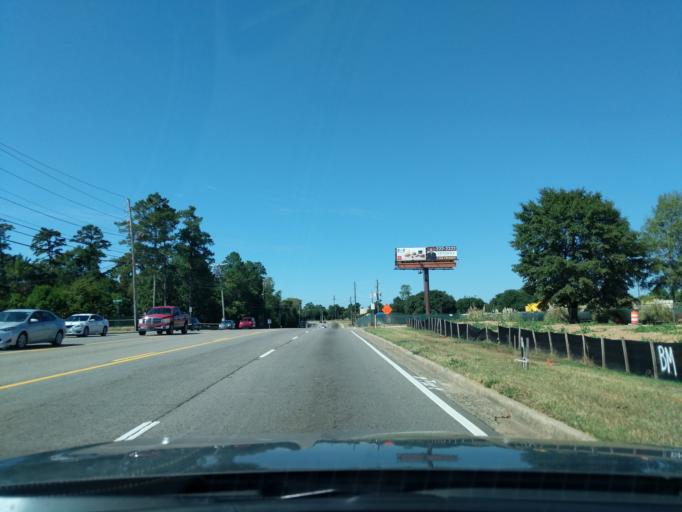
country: US
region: South Carolina
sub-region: Aiken County
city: North Augusta
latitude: 33.5015
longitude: -82.0136
